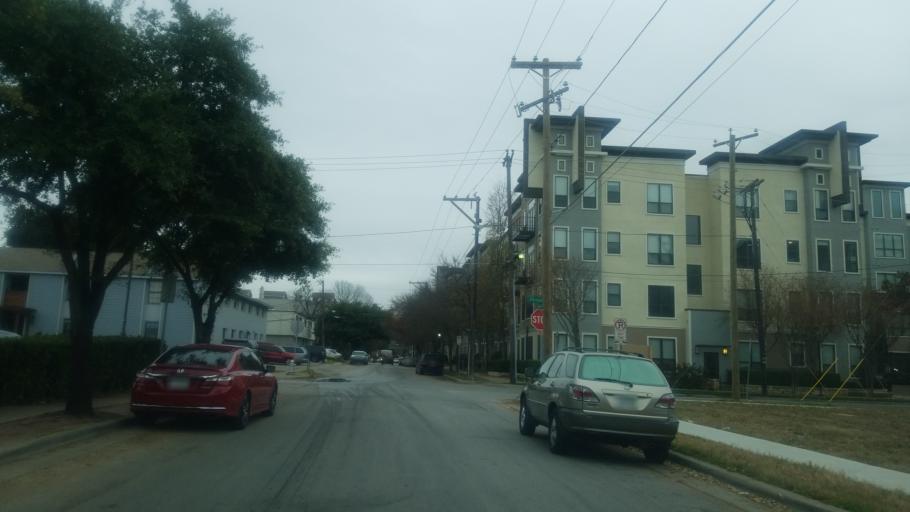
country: US
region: Texas
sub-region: Dallas County
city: Dallas
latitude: 32.8077
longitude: -96.8141
